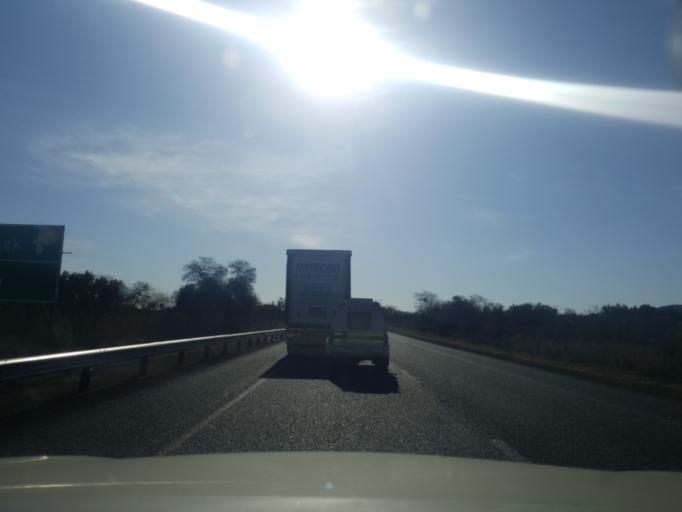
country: ZA
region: North-West
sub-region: Ngaka Modiri Molema District Municipality
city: Zeerust
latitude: -25.5338
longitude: 26.0247
